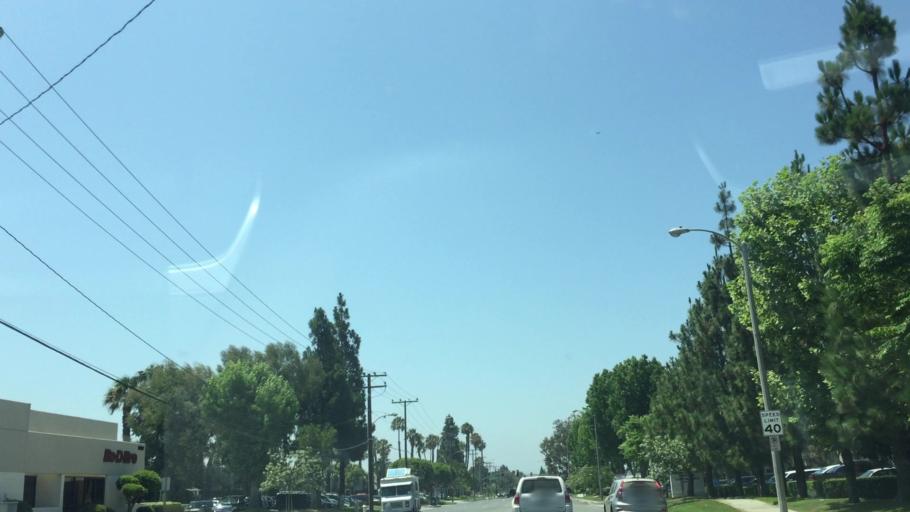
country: US
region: California
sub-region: Orange County
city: Fountain Valley
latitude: 33.7153
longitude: -117.9285
